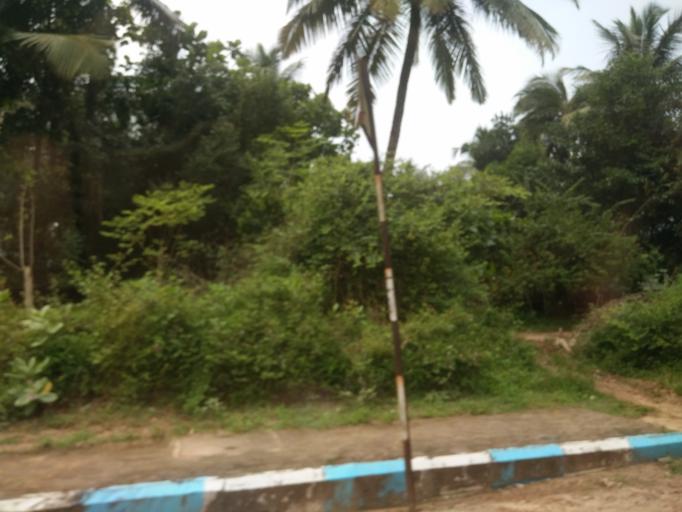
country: IN
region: Goa
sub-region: South Goa
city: Chinchinim
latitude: 15.2447
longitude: 73.9723
